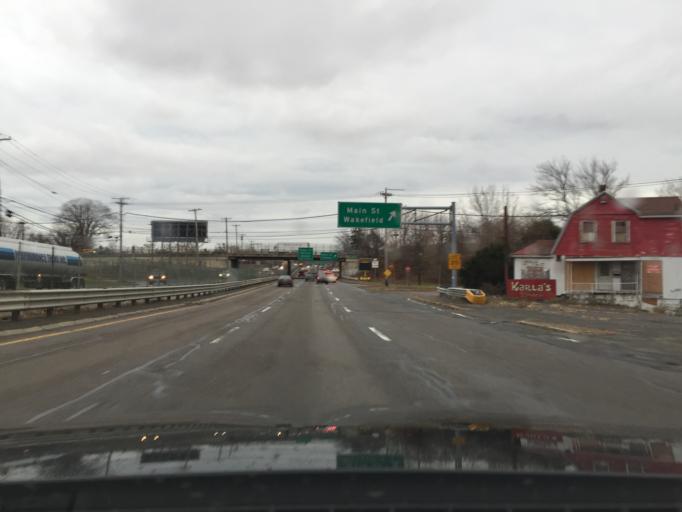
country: US
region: Massachusetts
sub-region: Essex County
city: Saugus
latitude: 42.4663
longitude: -71.0254
